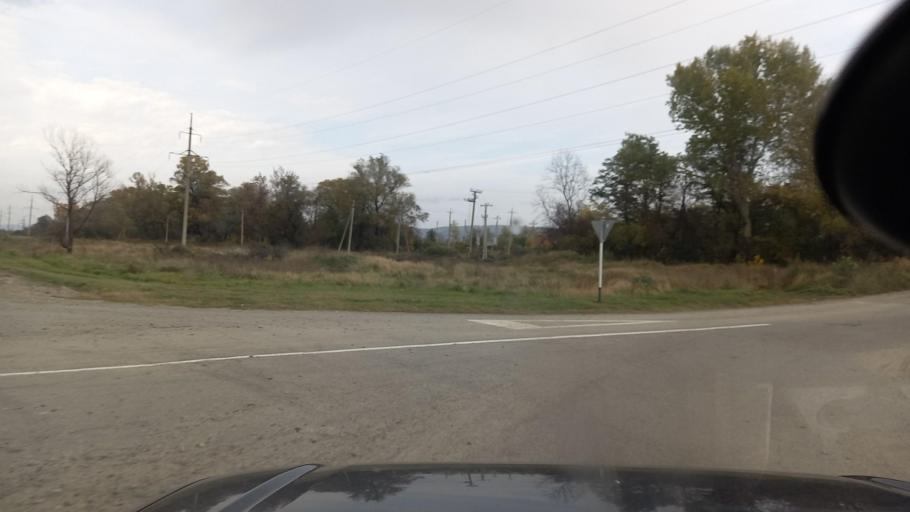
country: RU
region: Krasnodarskiy
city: Shedok
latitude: 44.1838
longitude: 40.8423
